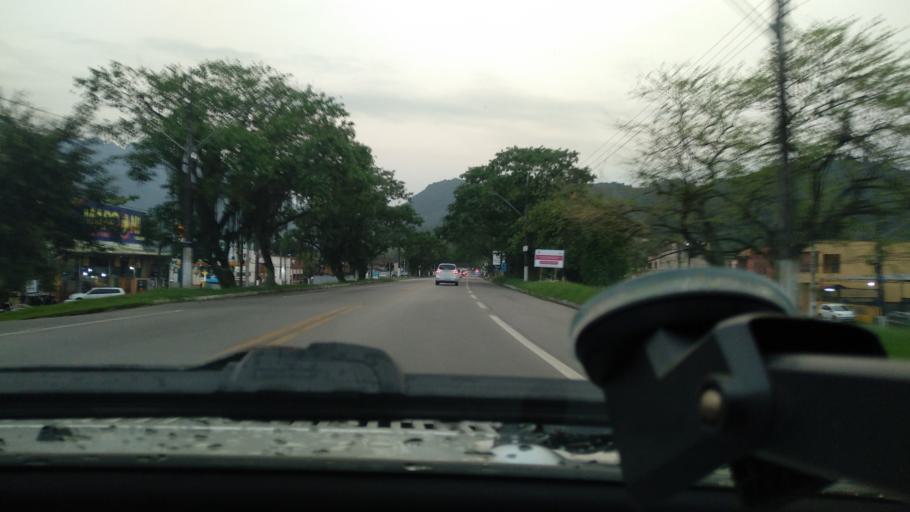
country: BR
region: Rio de Janeiro
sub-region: Angra Dos Reis
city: Angra dos Reis
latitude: -23.0211
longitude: -44.5351
